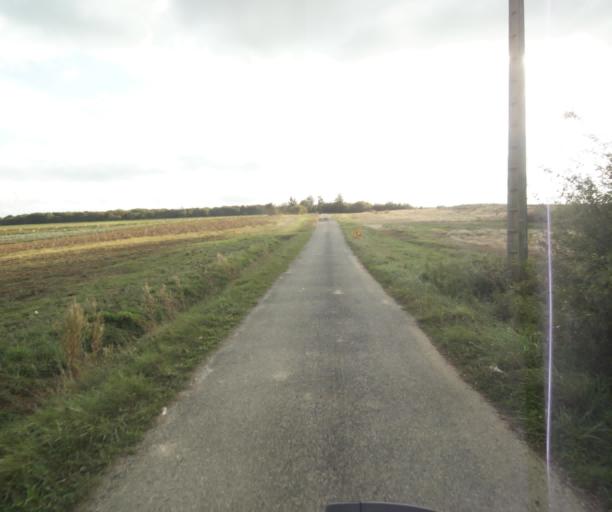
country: FR
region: Midi-Pyrenees
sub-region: Departement de la Haute-Garonne
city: Launac
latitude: 43.8023
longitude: 1.1179
